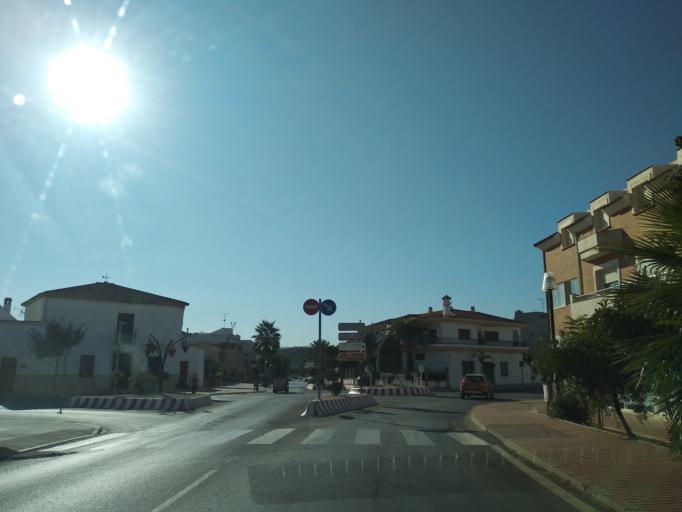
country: ES
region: Andalusia
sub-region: Provincia de Malaga
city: Mollina
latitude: 37.1213
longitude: -4.6596
